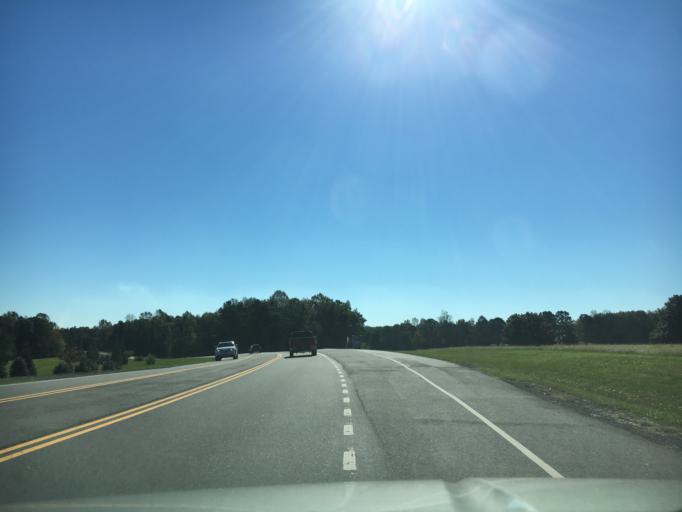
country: US
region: Virginia
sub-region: Goochland County
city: Goochland
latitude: 37.6994
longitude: -77.8330
